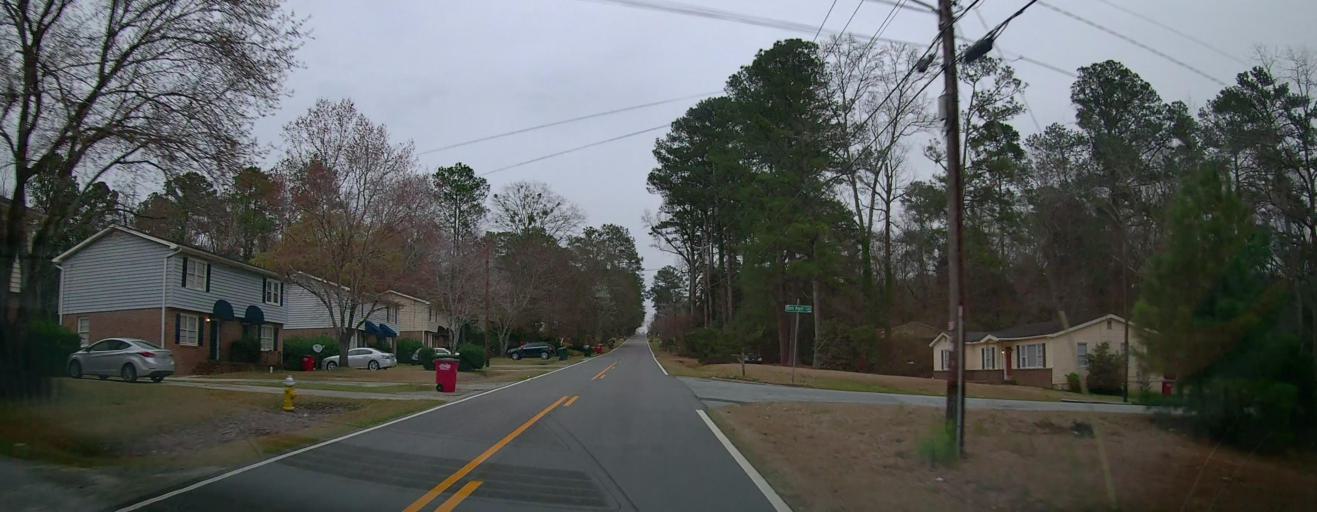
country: US
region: Georgia
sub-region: Bibb County
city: Macon
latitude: 32.8592
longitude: -83.7022
